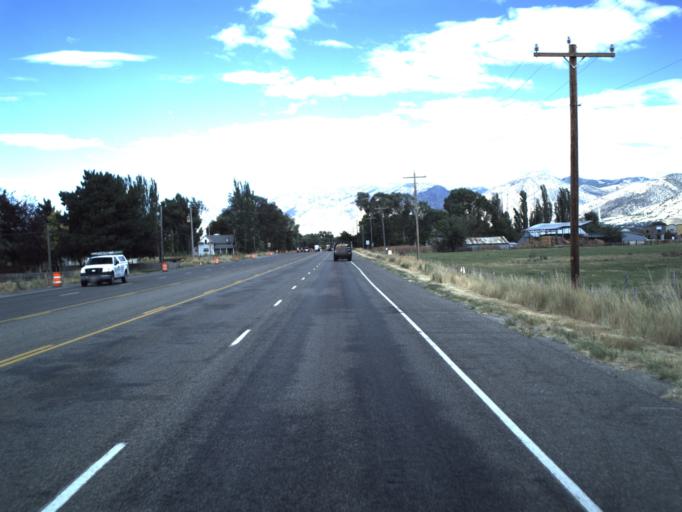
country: US
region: Utah
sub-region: Cache County
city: Nibley
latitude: 41.6870
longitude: -111.8715
